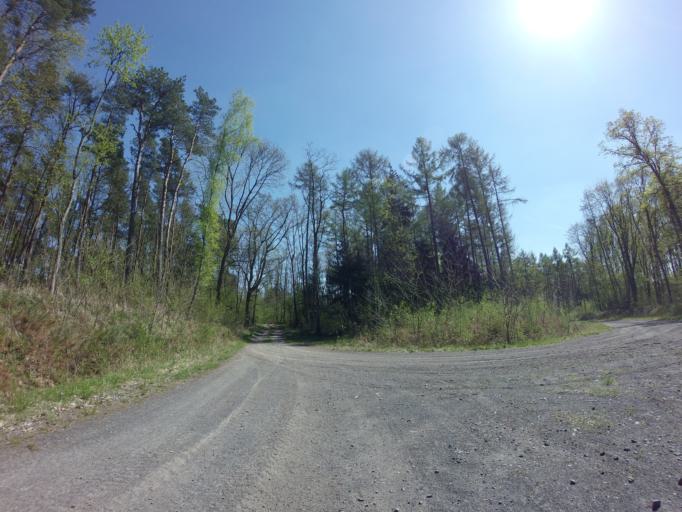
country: PL
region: West Pomeranian Voivodeship
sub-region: Powiat choszczenski
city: Choszczno
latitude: 53.1820
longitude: 15.3604
